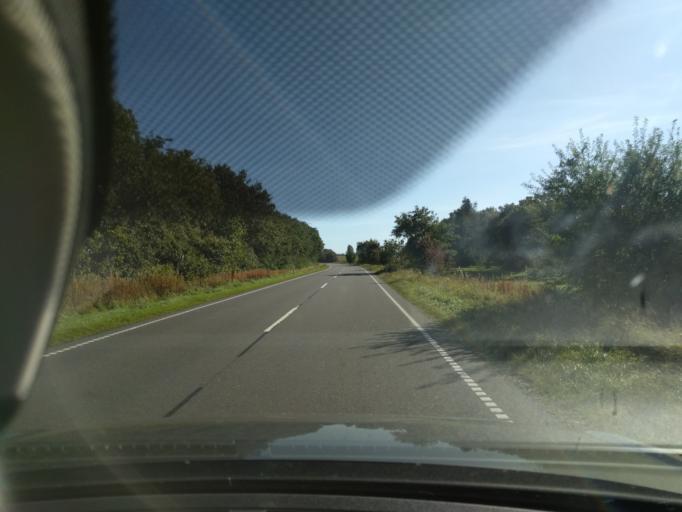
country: DK
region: North Denmark
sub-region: Vesthimmerland Kommune
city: Farso
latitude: 56.7223
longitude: 9.2660
